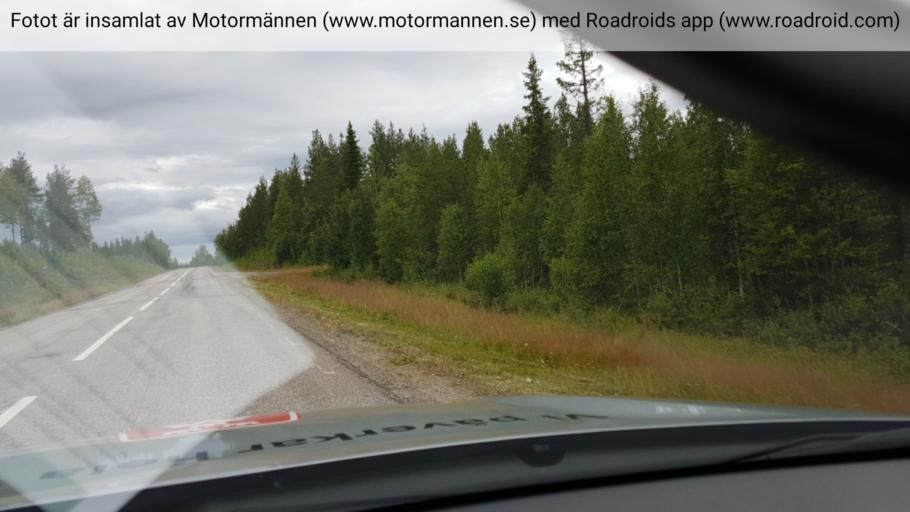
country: SE
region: Norrbotten
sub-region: Overkalix Kommun
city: OEverkalix
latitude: 66.8055
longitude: 22.9734
